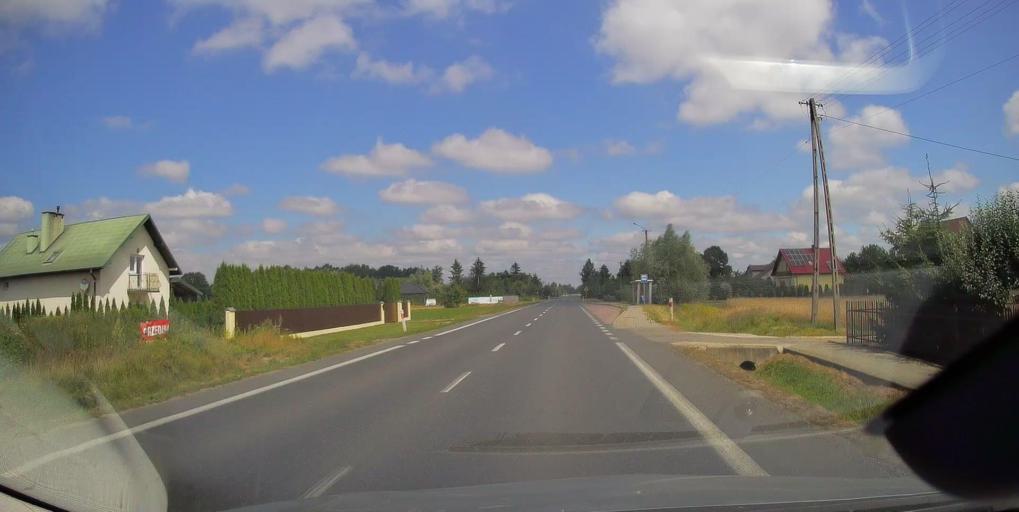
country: PL
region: Subcarpathian Voivodeship
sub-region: Powiat mielecki
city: Przeclaw
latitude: 50.1733
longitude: 21.4921
